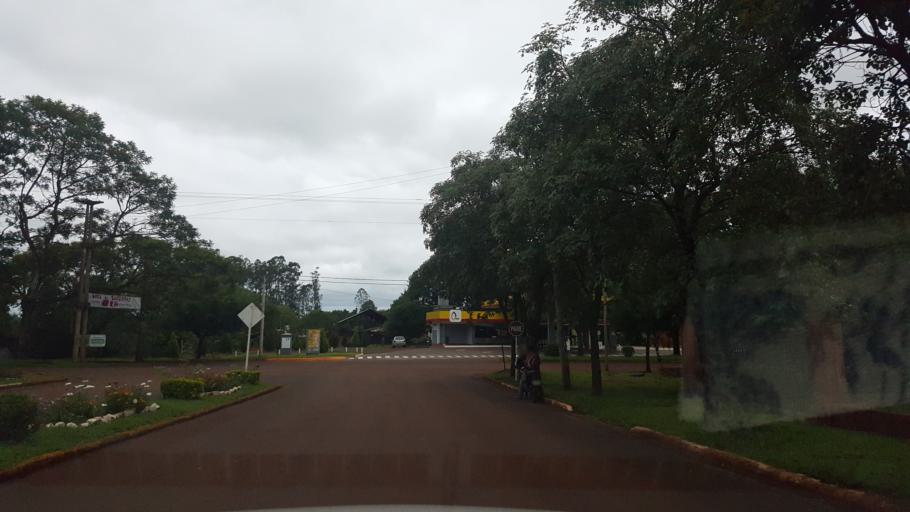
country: AR
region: Misiones
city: Ruiz de Montoya
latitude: -26.9682
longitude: -55.0573
